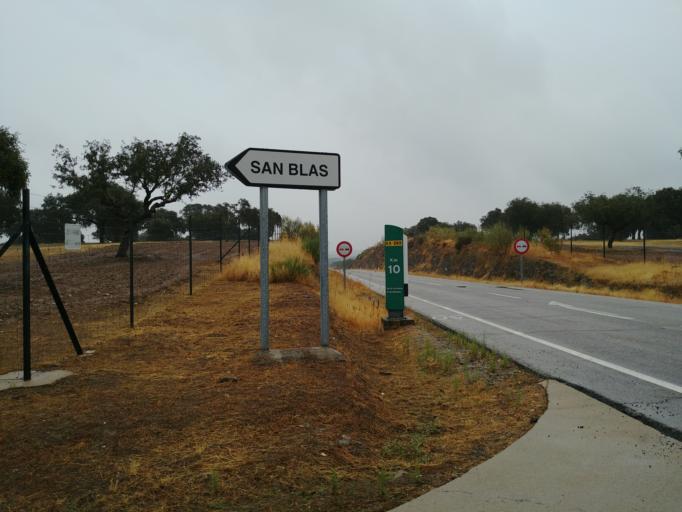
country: ES
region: Extremadura
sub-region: Provincia de Caceres
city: Jaraicejo
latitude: 39.6949
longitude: -5.9191
